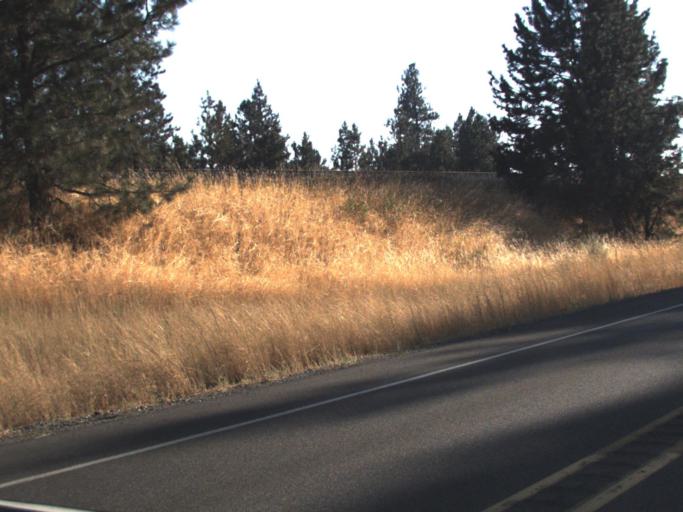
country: US
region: Washington
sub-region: Spokane County
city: Otis Orchards-East Farms
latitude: 47.7217
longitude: -117.0745
